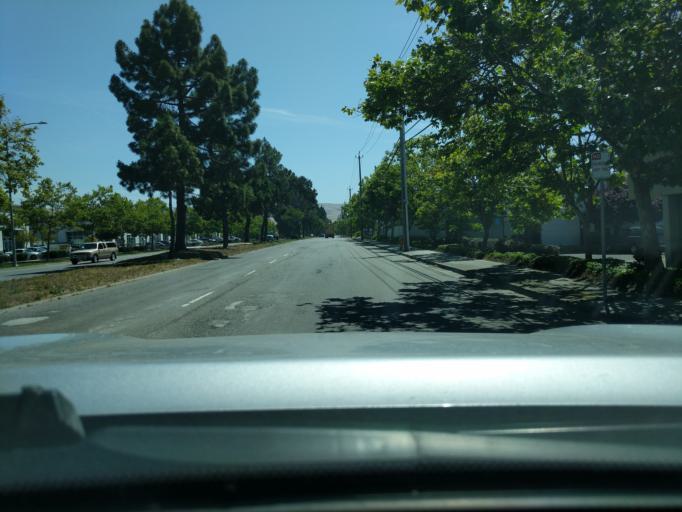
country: US
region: California
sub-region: Alameda County
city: Hayward
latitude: 37.6175
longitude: -122.0688
